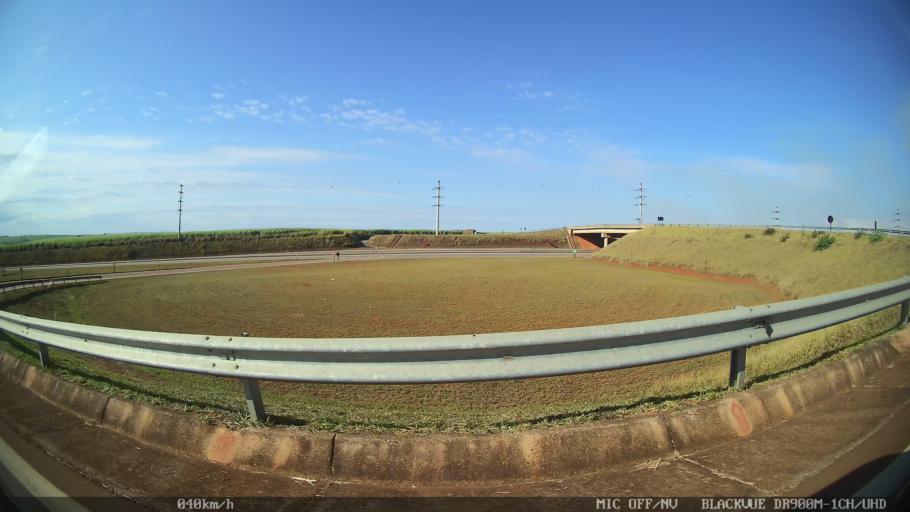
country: BR
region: Sao Paulo
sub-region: Piracicaba
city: Piracicaba
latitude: -22.6804
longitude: -47.5963
